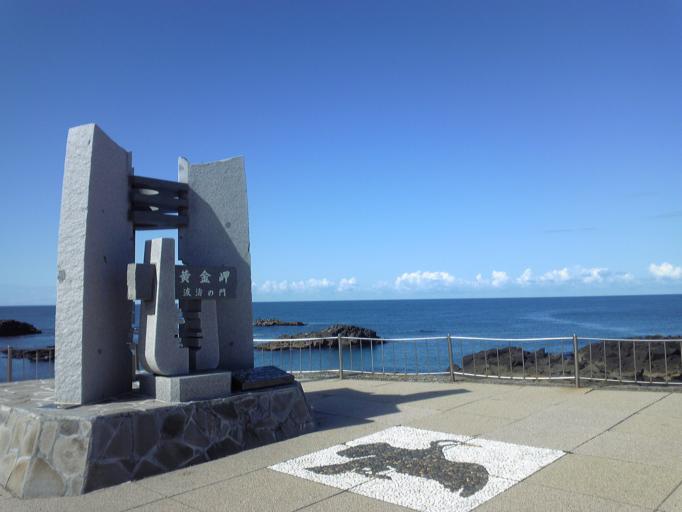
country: JP
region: Hokkaido
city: Rumoi
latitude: 43.9465
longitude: 141.6291
